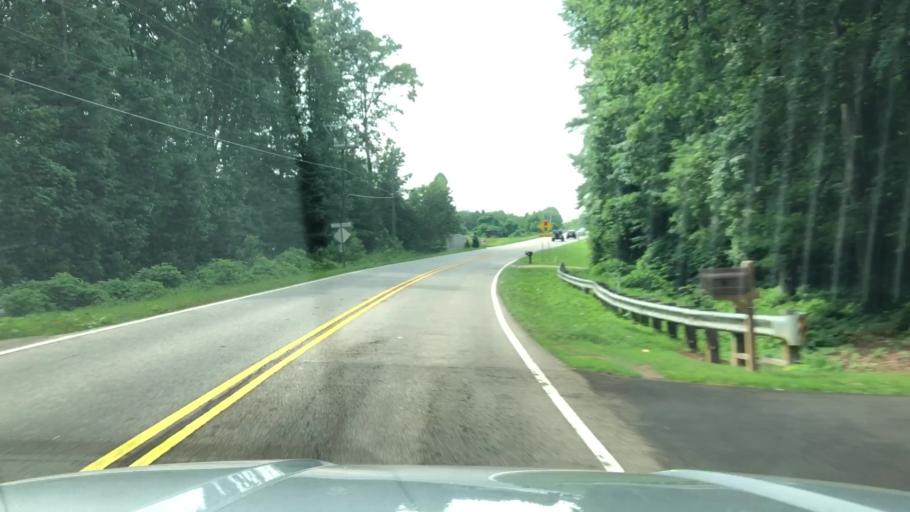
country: US
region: Georgia
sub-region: Paulding County
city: Hiram
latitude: 33.9407
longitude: -84.7638
